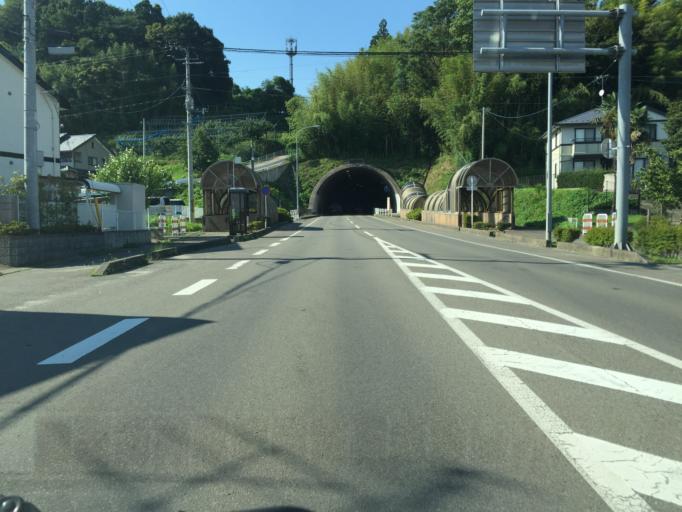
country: JP
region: Fukushima
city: Fukushima-shi
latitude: 37.8289
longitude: 140.4447
